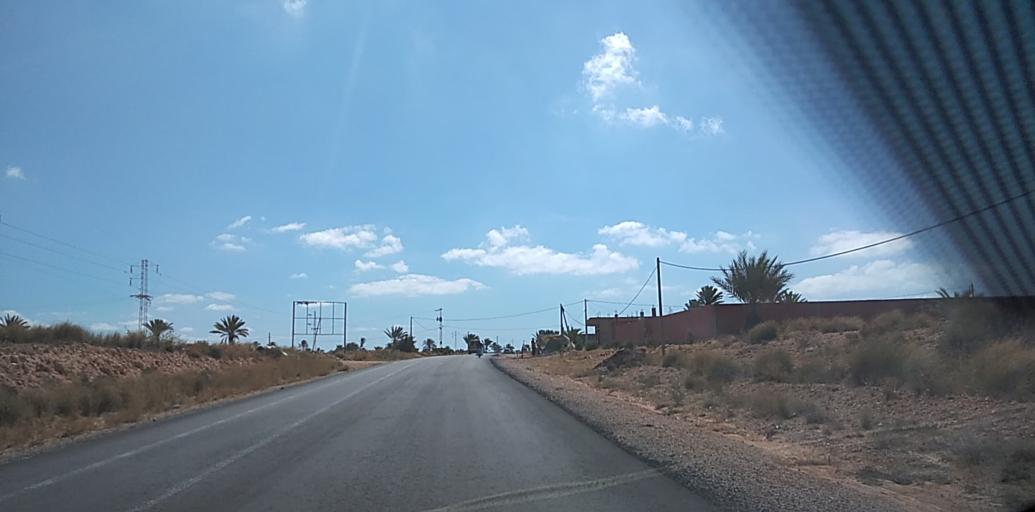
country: TN
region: Safaqis
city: Al Qarmadah
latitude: 34.6576
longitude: 11.0806
